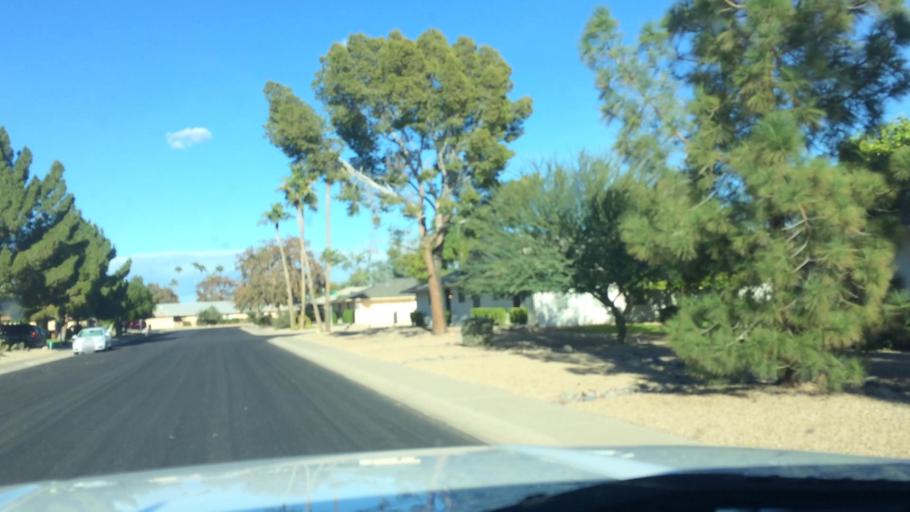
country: US
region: Arizona
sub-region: Maricopa County
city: Sun City West
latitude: 33.6546
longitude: -112.3377
